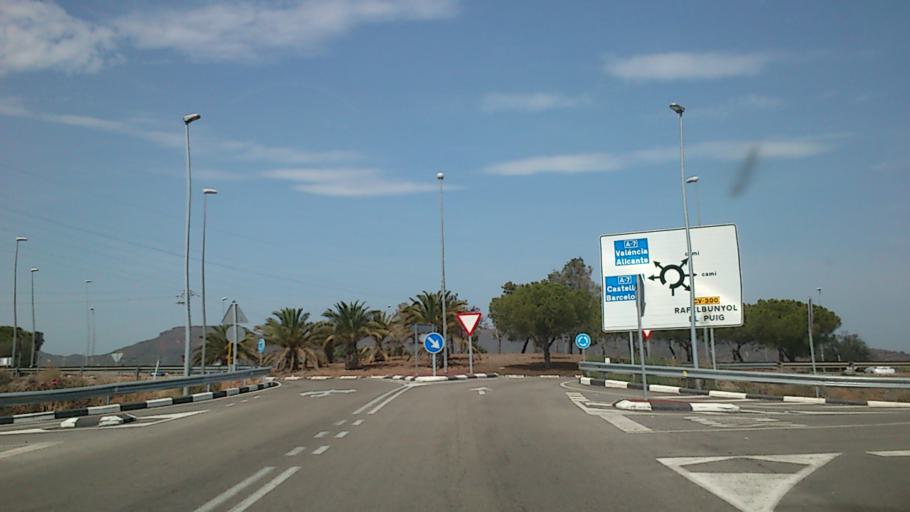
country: ES
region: Valencia
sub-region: Provincia de Valencia
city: Museros
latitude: 39.6078
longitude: -0.3439
